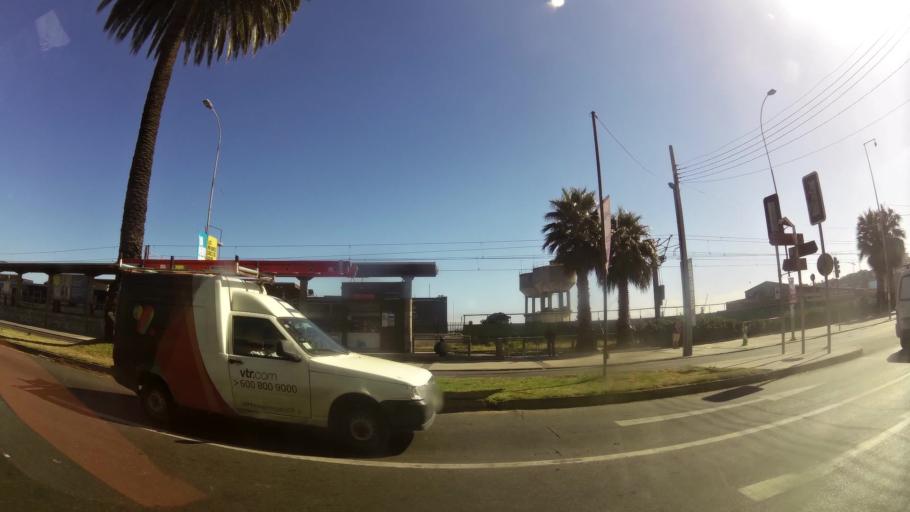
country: CL
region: Valparaiso
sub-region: Provincia de Valparaiso
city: Valparaiso
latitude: -33.0443
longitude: -71.6122
